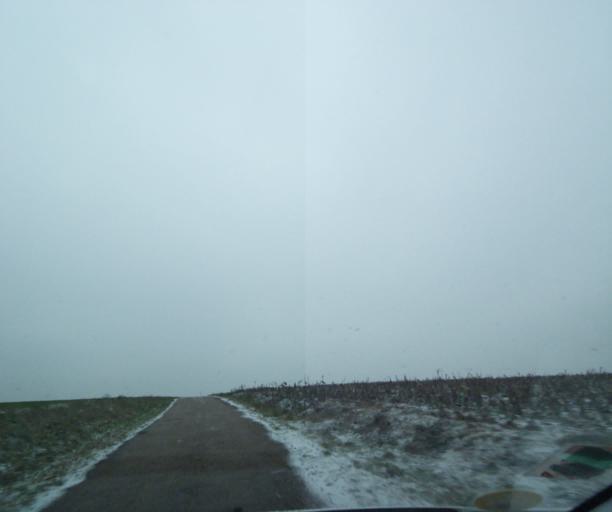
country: FR
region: Champagne-Ardenne
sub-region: Departement de la Haute-Marne
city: Wassy
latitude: 48.4664
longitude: 5.0045
